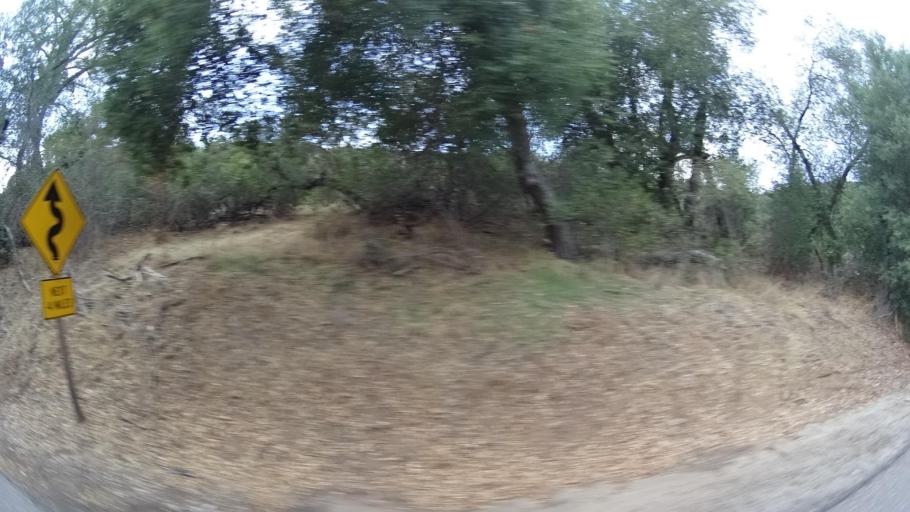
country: US
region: California
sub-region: San Diego County
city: Ramona
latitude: 32.9974
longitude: -116.9302
